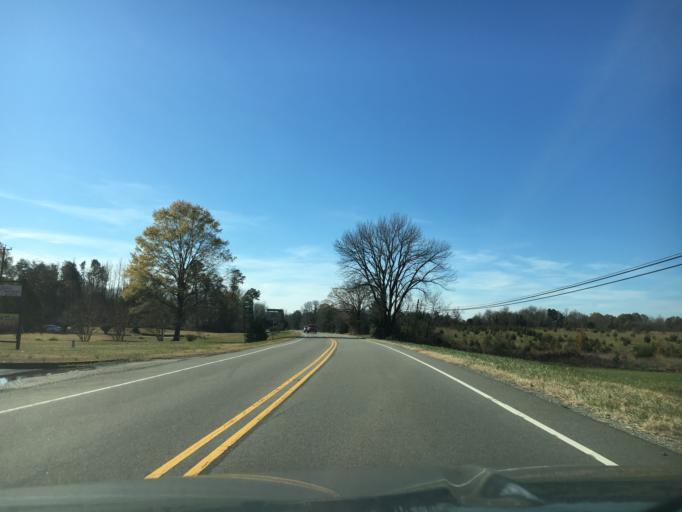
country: US
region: Virginia
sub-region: Cumberland County
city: Cumberland
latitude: 37.5085
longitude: -78.2338
